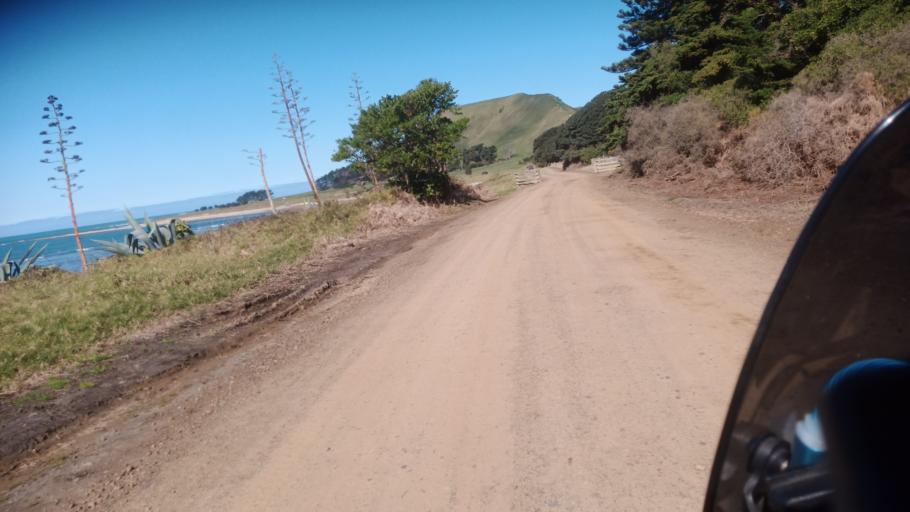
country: NZ
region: Gisborne
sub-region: Gisborne District
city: Gisborne
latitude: -39.0972
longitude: 177.9637
